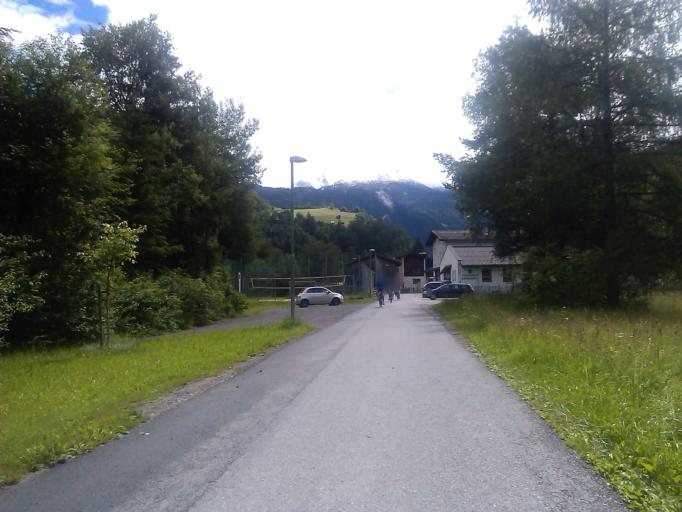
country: AT
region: Tyrol
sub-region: Politischer Bezirk Landeck
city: Zams
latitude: 47.1168
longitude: 10.6078
